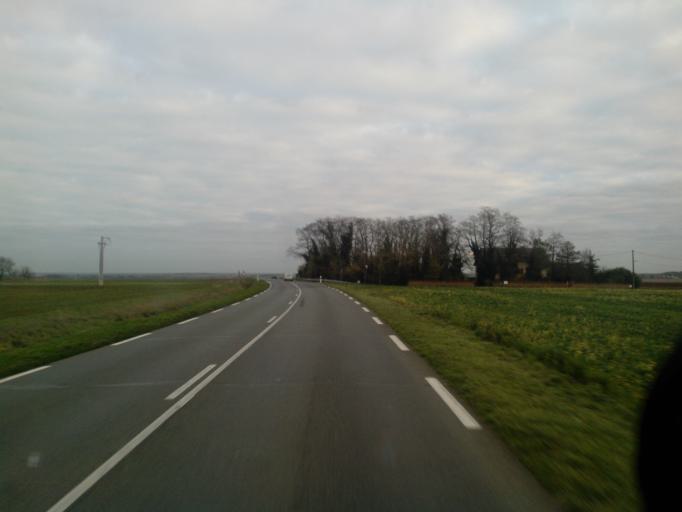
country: FR
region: Poitou-Charentes
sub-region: Departement de la Vienne
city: Cisse
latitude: 46.6317
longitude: 0.2403
